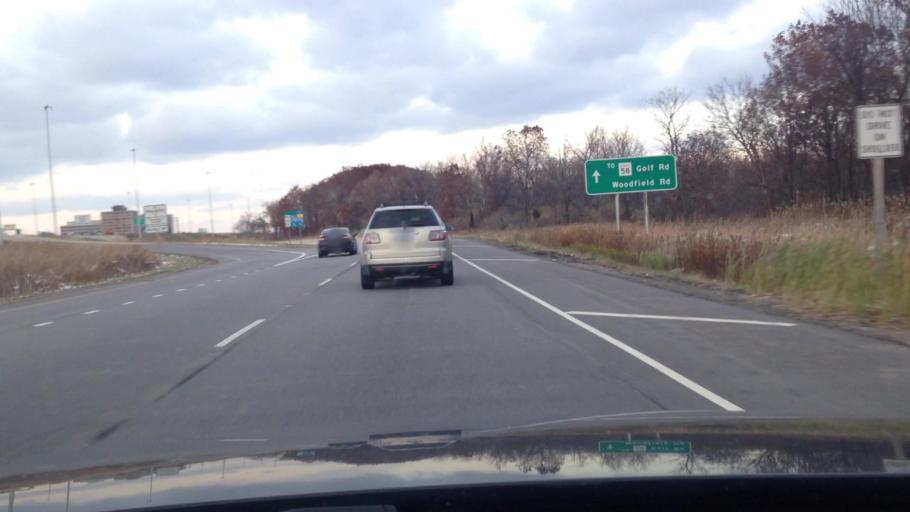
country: US
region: Illinois
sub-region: Cook County
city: Rolling Meadows
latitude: 42.0375
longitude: -88.0293
